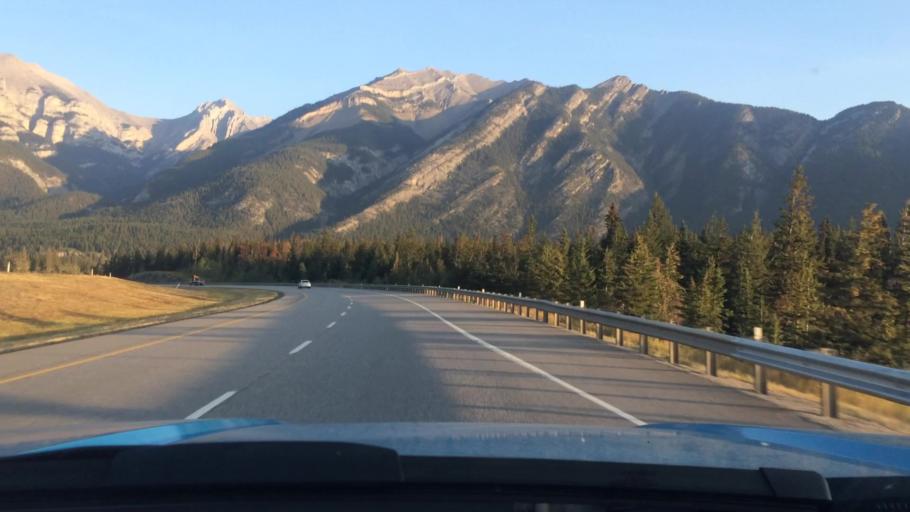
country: CA
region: Alberta
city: Canmore
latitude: 51.0526
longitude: -115.1904
